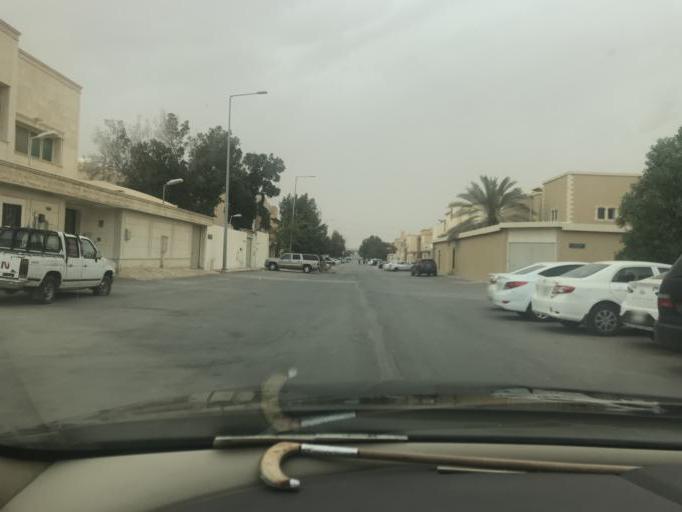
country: SA
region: Ar Riyad
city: Riyadh
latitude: 24.7921
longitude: 46.6940
